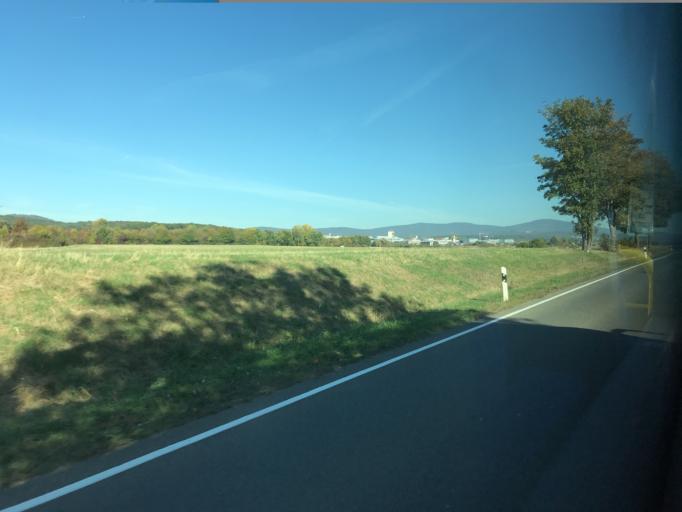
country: DE
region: Hesse
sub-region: Regierungsbezirk Darmstadt
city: Kriftel
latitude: 50.1063
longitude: 8.4704
